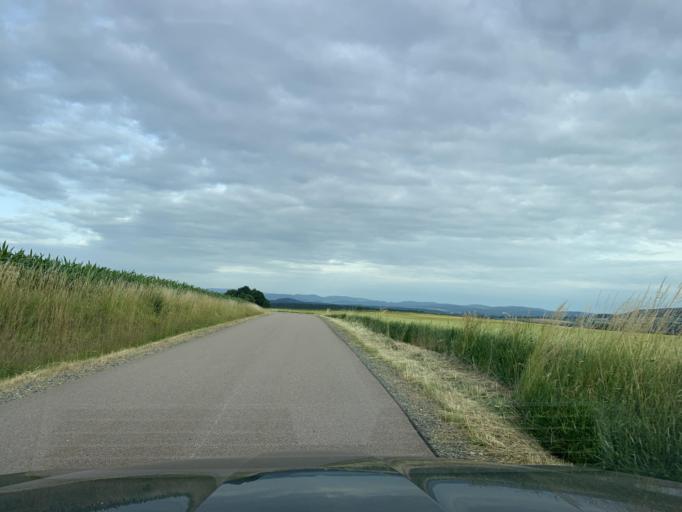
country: DE
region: Bavaria
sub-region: Upper Palatinate
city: Thanstein
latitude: 49.4073
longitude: 12.4538
